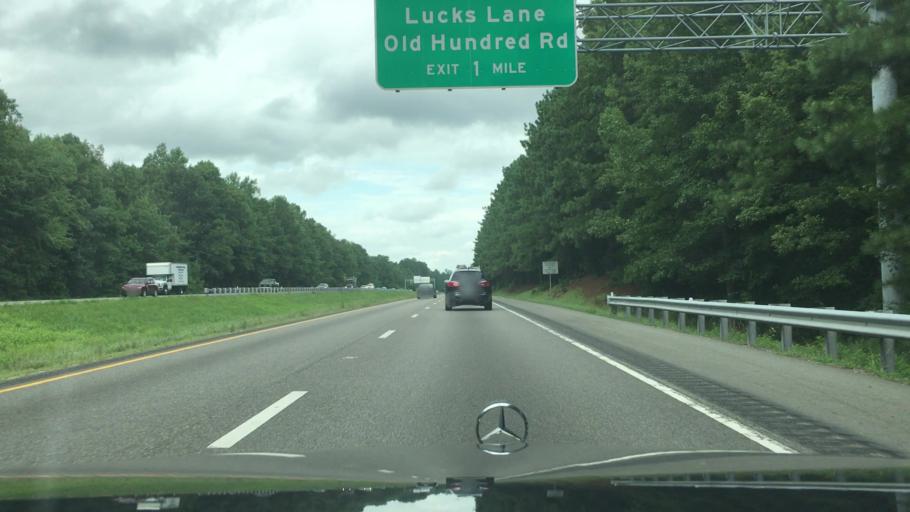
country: US
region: Virginia
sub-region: Chesterfield County
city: Brandermill
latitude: 37.4356
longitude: -77.6343
